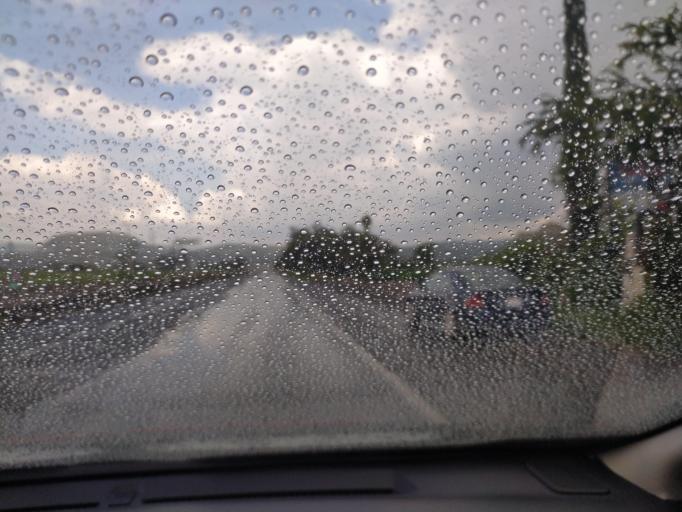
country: MX
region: Jalisco
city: Bellavista
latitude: 20.4195
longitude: -103.6181
